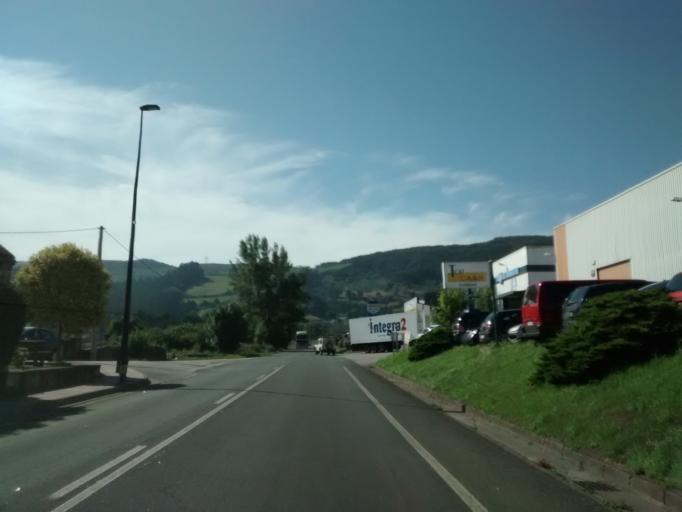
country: ES
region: Cantabria
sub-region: Provincia de Cantabria
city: Cartes
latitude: 43.3206
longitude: -4.0694
